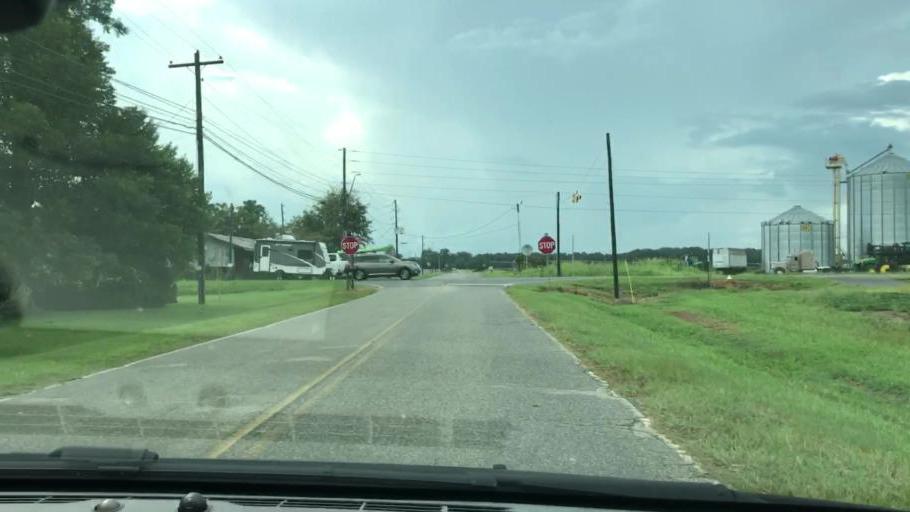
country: US
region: Georgia
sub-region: Early County
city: Blakely
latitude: 31.3749
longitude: -84.9565
